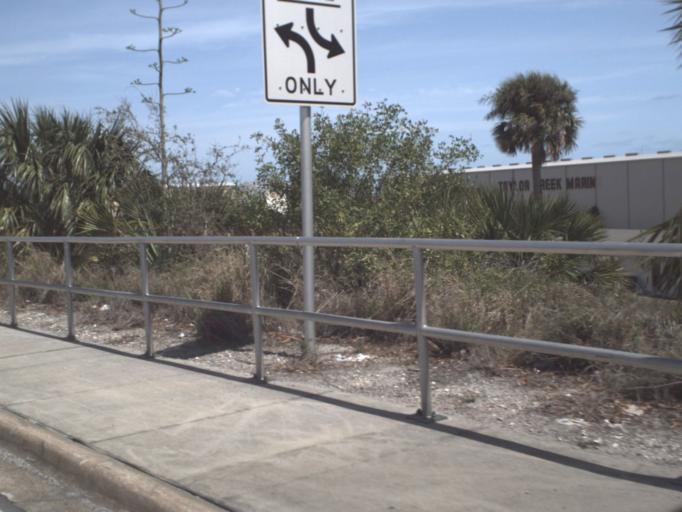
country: US
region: Florida
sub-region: Saint Lucie County
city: Fort Pierce
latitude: 27.4635
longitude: -80.3300
